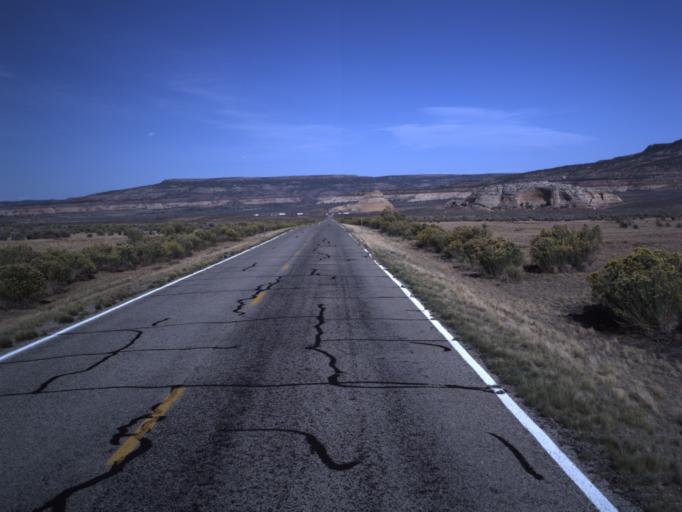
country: US
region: Utah
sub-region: San Juan County
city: Monticello
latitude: 38.0661
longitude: -109.3803
